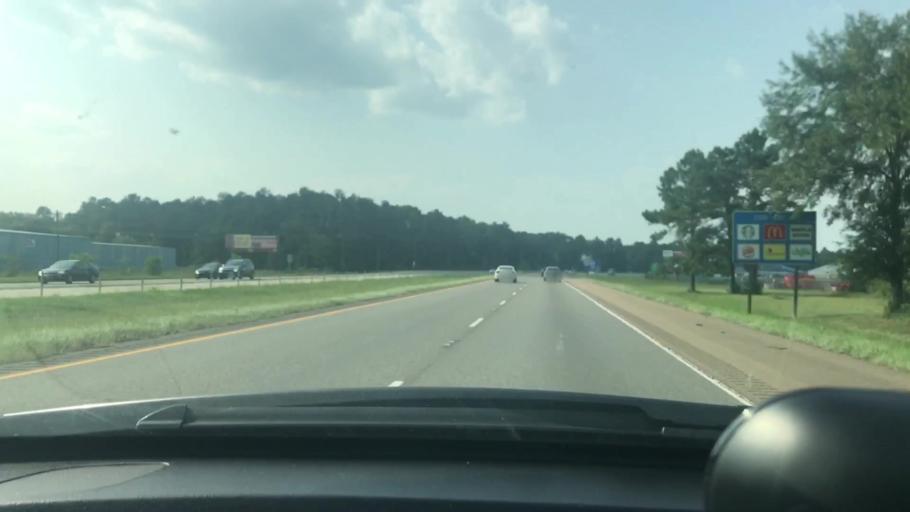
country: US
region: Louisiana
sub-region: Tangipahoa Parish
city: Hammond
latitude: 30.4965
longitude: -90.5013
